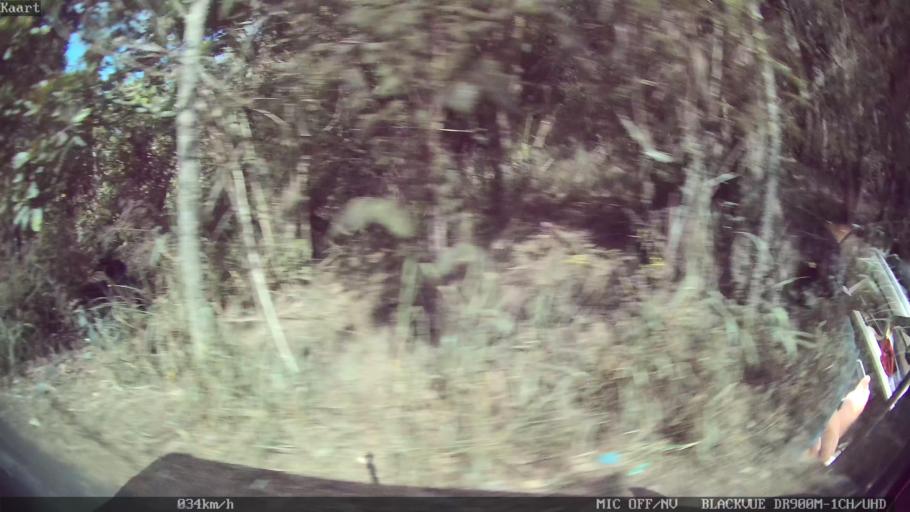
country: ID
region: Bali
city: Banjar Kedisan
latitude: -8.2287
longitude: 115.3588
